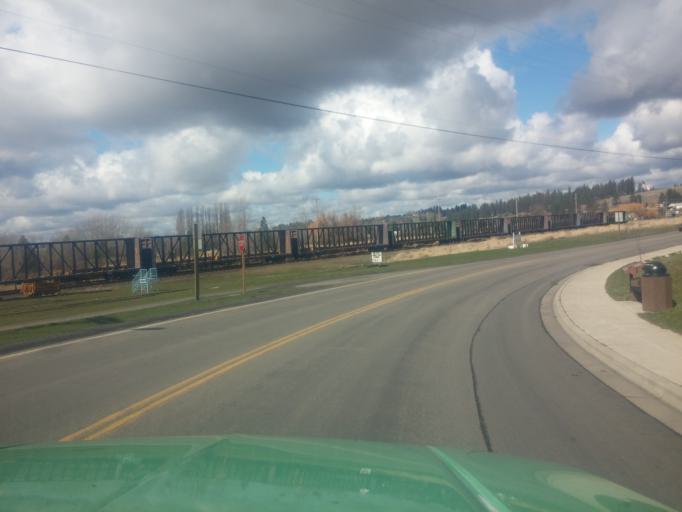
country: US
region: Idaho
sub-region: Latah County
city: Moscow
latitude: 46.9218
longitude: -116.9012
